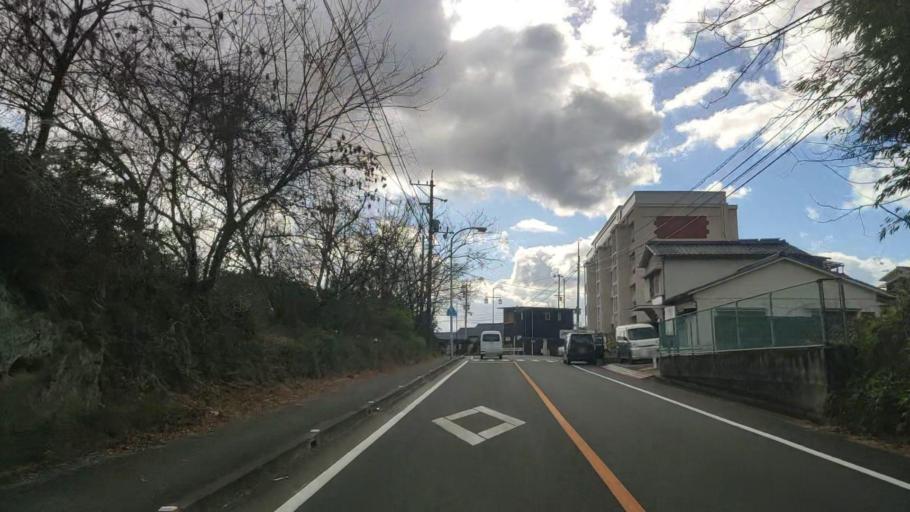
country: JP
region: Ehime
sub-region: Shikoku-chuo Shi
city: Matsuyama
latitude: 33.8785
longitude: 132.7035
